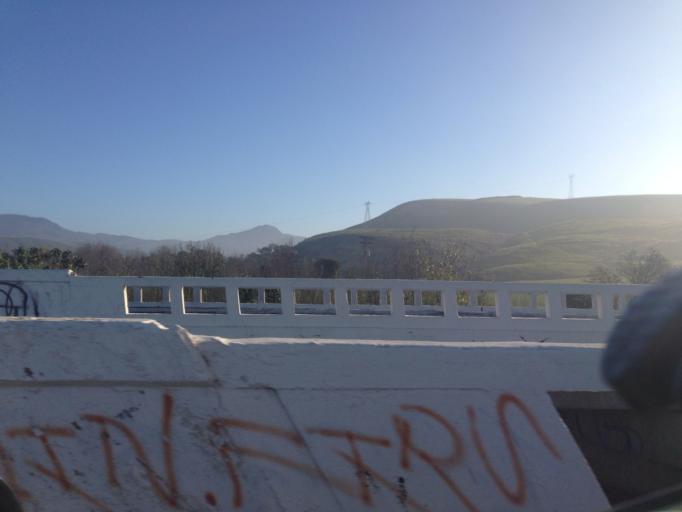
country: MX
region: Baja California
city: Primo Tapia
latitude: 32.2302
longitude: -116.9211
